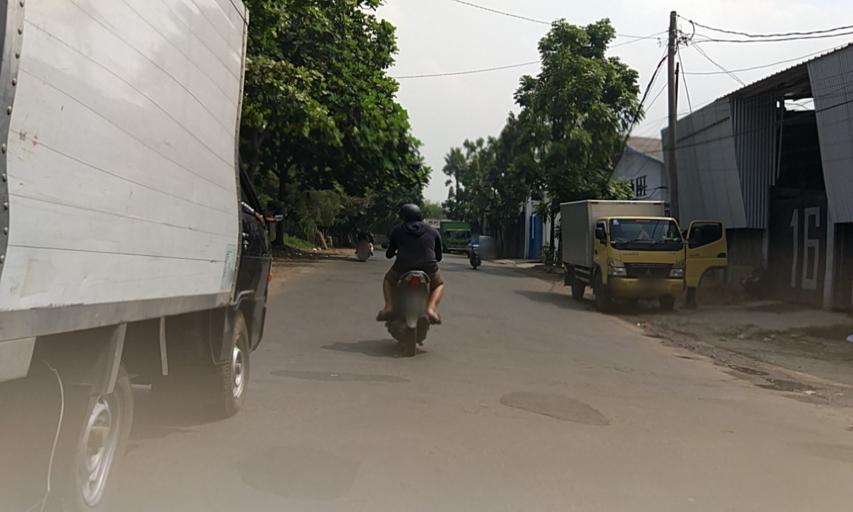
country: ID
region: West Java
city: Margahayukencana
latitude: -6.9503
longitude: 107.5629
